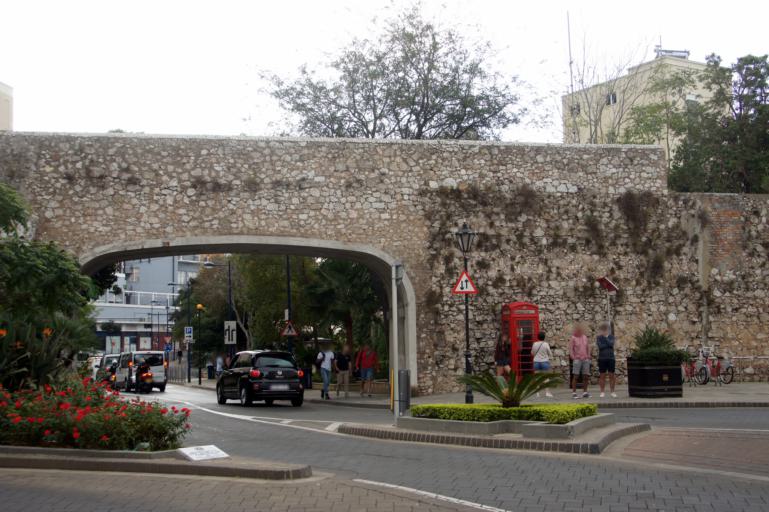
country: GI
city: Gibraltar
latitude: 36.1351
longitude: -5.3529
